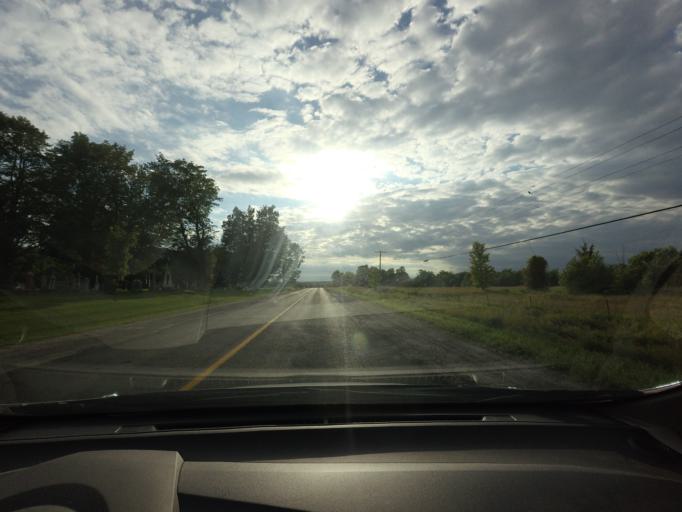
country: CA
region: Ontario
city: Perth
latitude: 44.6546
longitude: -76.4670
